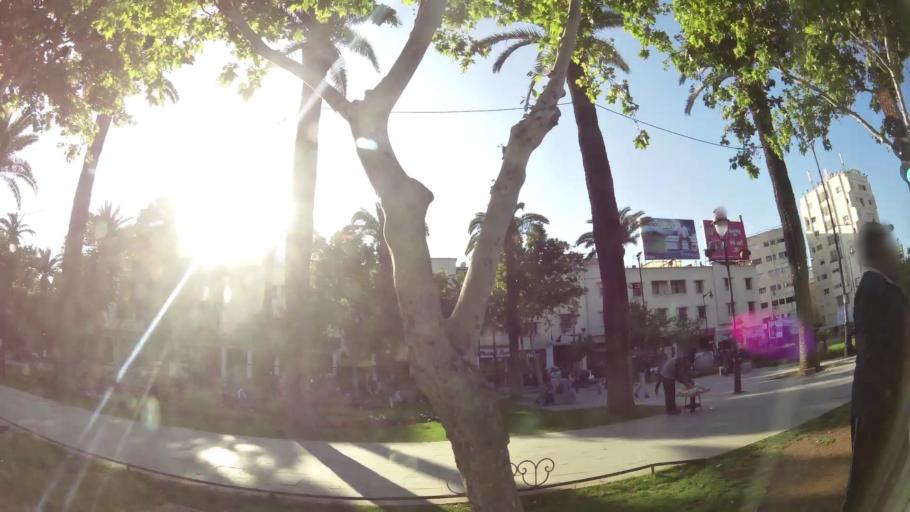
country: MA
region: Fes-Boulemane
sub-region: Fes
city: Fes
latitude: 34.0442
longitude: -4.9972
